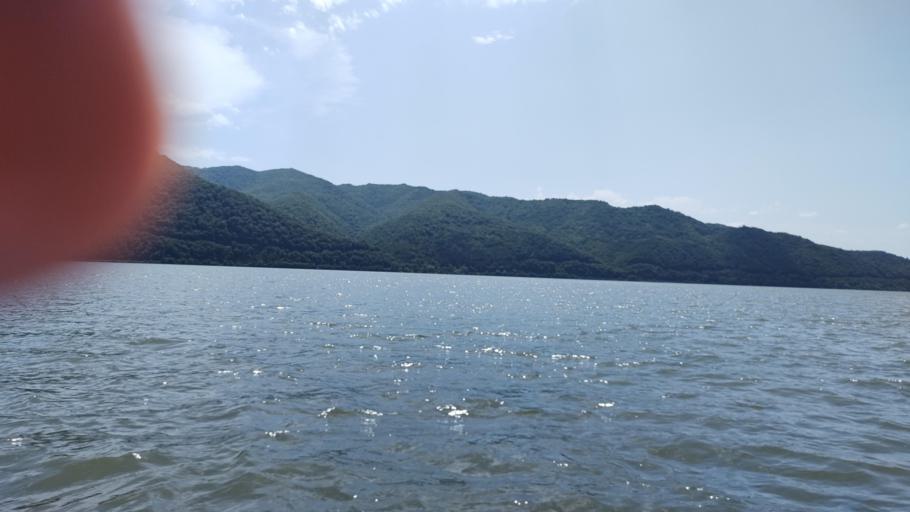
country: RO
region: Caras-Severin
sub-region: Comuna Berzasca
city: Liubcova
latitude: 44.6545
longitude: 21.8297
